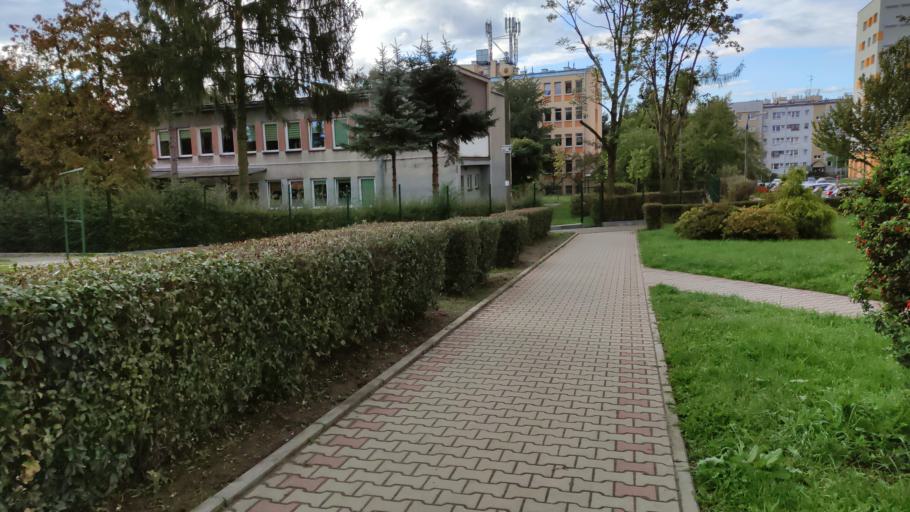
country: PL
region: Lesser Poland Voivodeship
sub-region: Powiat krakowski
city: Michalowice
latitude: 50.0995
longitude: 20.0146
